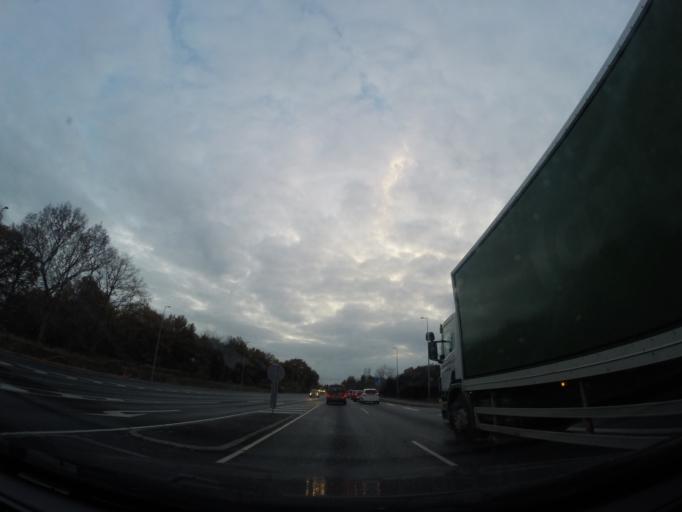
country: DK
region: Capital Region
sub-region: Ballerup Kommune
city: Ballerup
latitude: 55.7433
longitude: 12.3872
